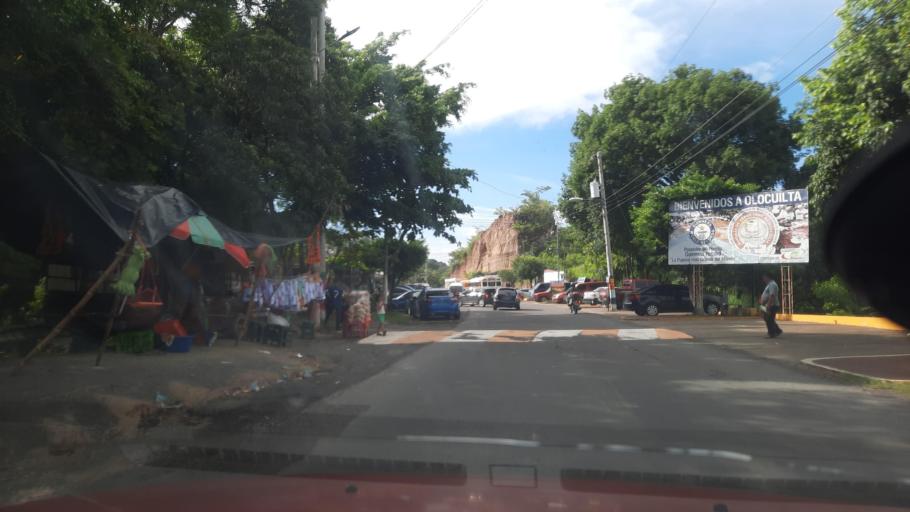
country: SV
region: La Paz
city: Olocuilta
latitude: 13.5647
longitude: -89.1178
